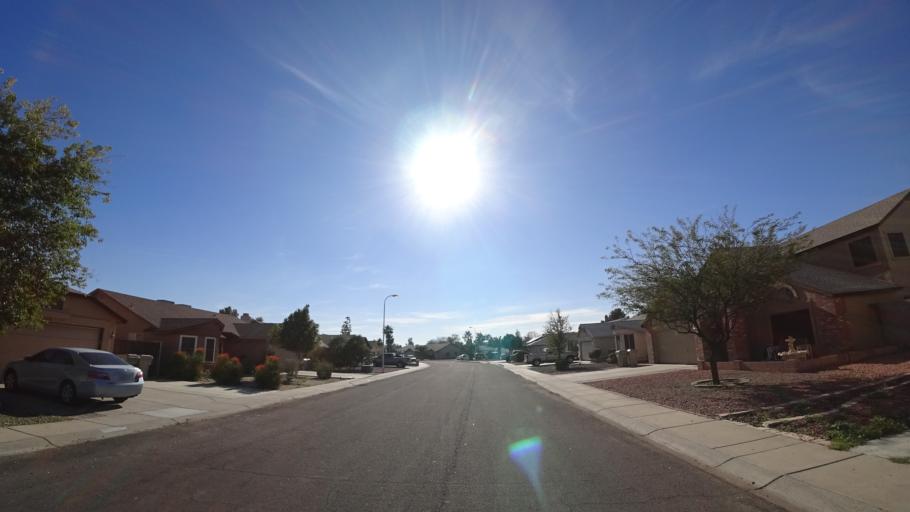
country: US
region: Arizona
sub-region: Maricopa County
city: Peoria
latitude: 33.5326
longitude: -112.2410
